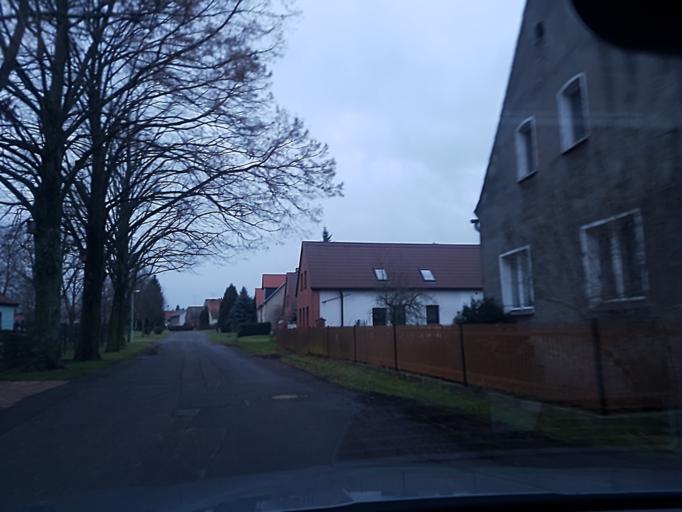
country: DE
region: Brandenburg
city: Schonborn
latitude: 51.5958
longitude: 13.5016
